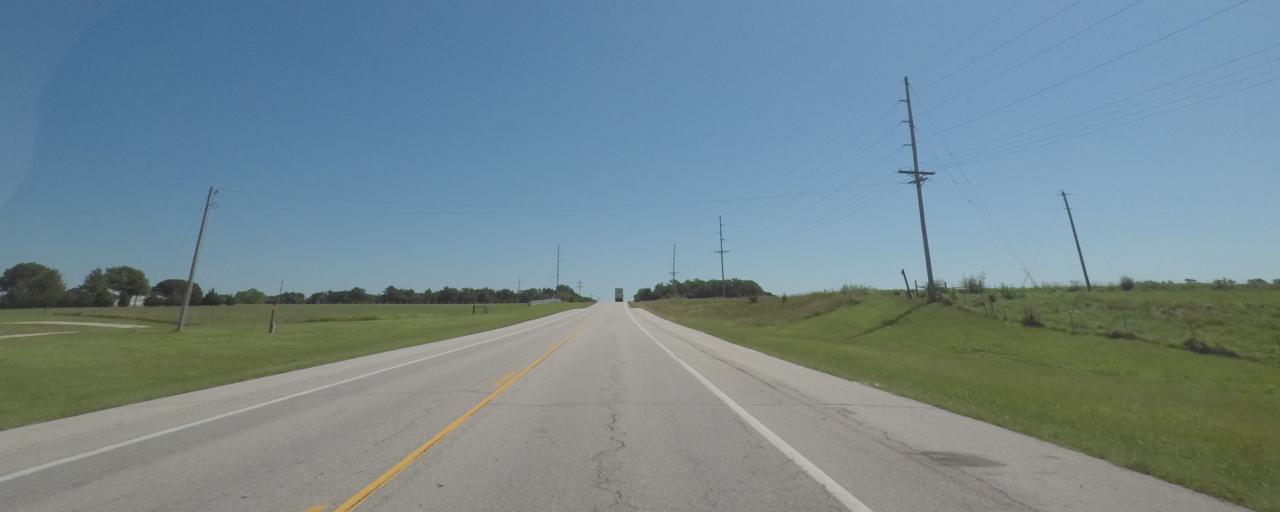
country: US
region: Kansas
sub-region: Sumner County
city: Belle Plaine
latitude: 37.3912
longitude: -97.3768
